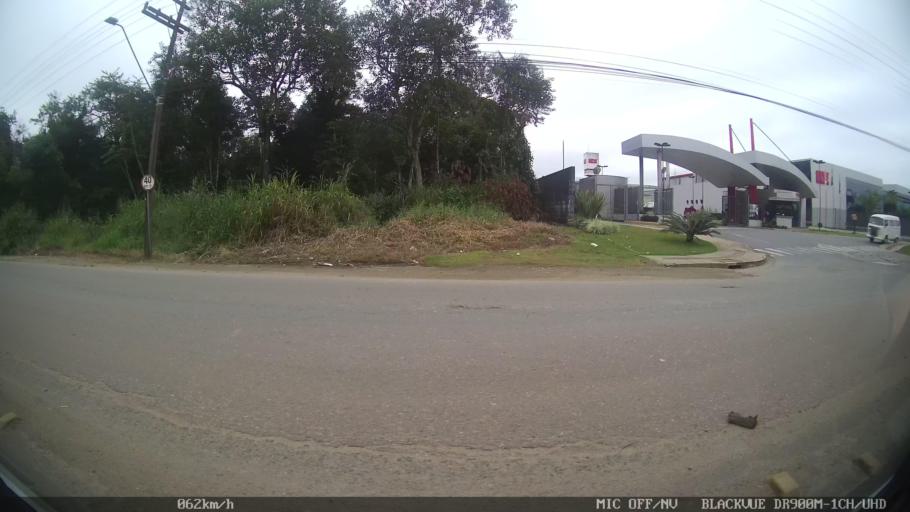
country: BR
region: Santa Catarina
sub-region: Joinville
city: Joinville
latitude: -26.2224
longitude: -48.9048
